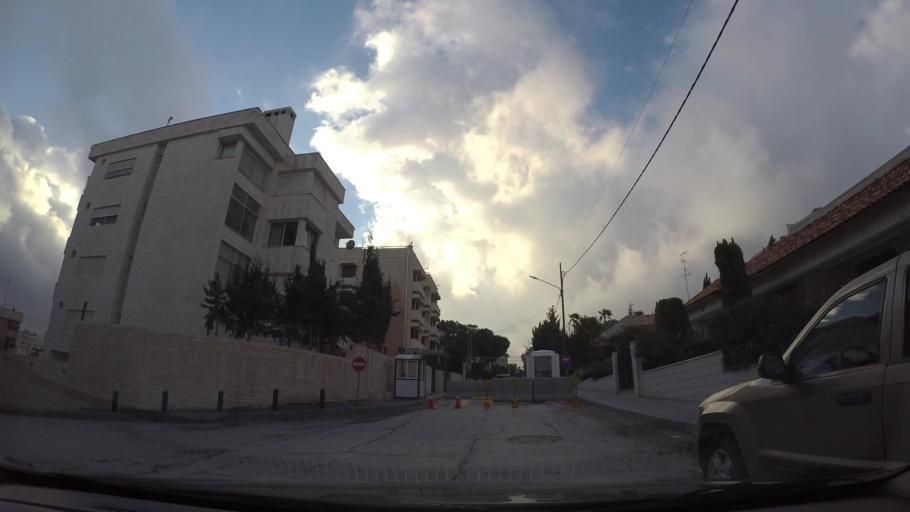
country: JO
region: Amman
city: Amman
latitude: 31.9553
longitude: 35.8909
